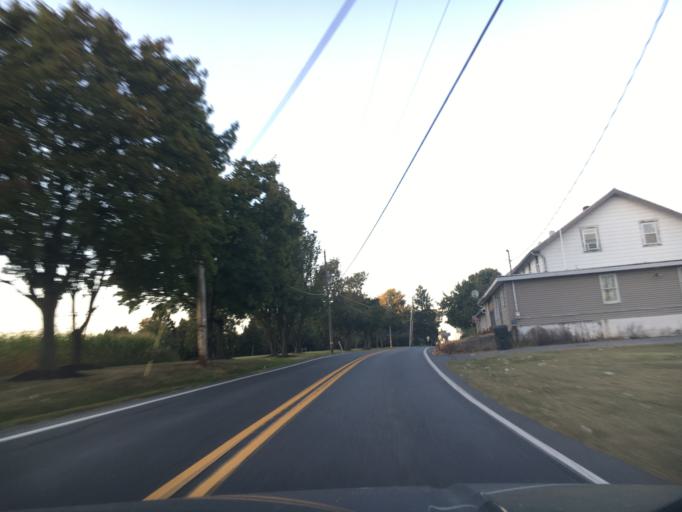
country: US
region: Pennsylvania
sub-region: Lehigh County
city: Schnecksville
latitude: 40.6485
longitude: -75.5779
